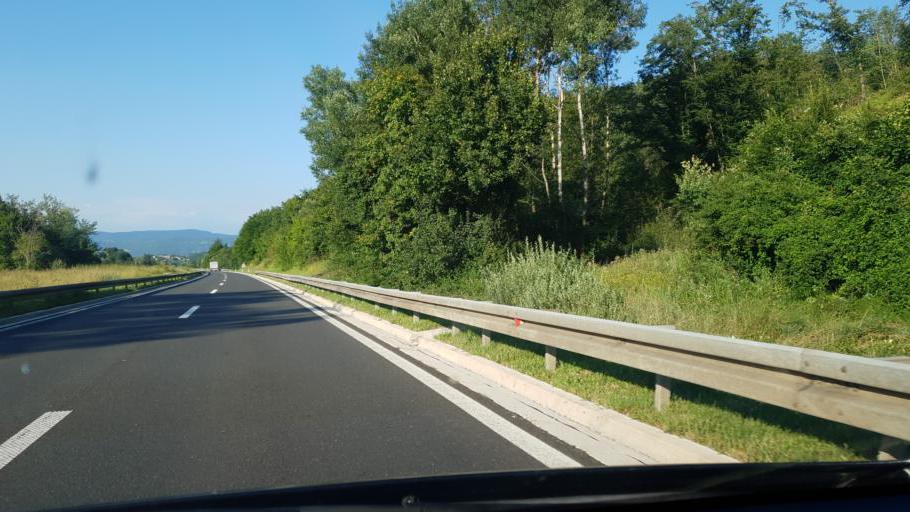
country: HR
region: Istarska
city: Pazin
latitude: 45.2936
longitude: 14.0414
